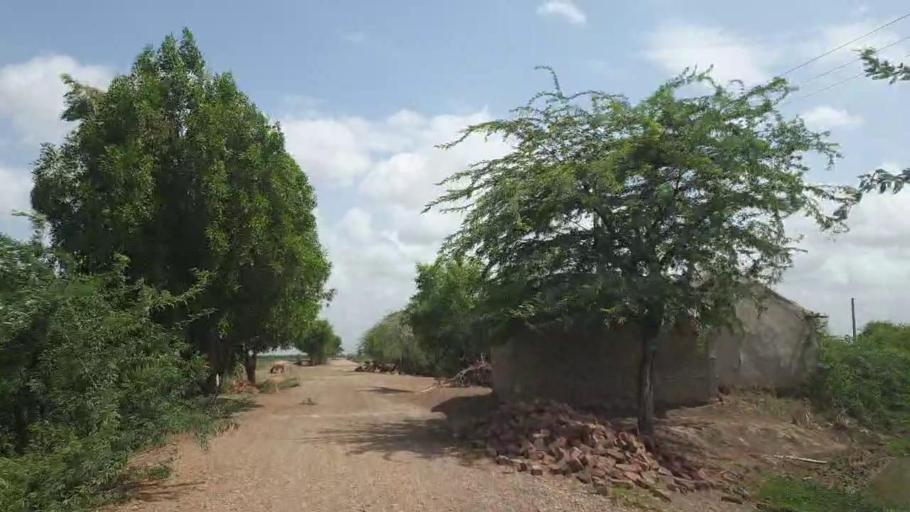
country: PK
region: Sindh
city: Tando Bago
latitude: 24.6501
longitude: 68.9933
